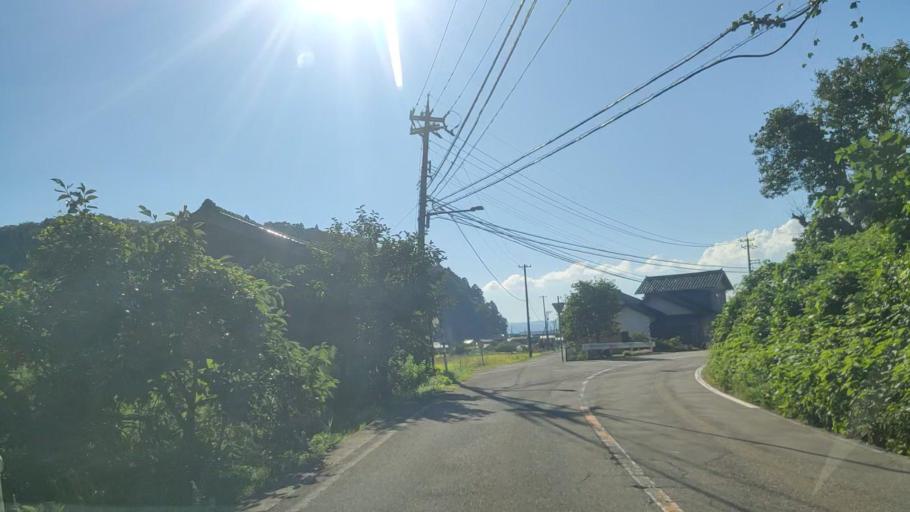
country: JP
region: Ishikawa
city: Nanao
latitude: 37.2341
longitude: 136.9722
